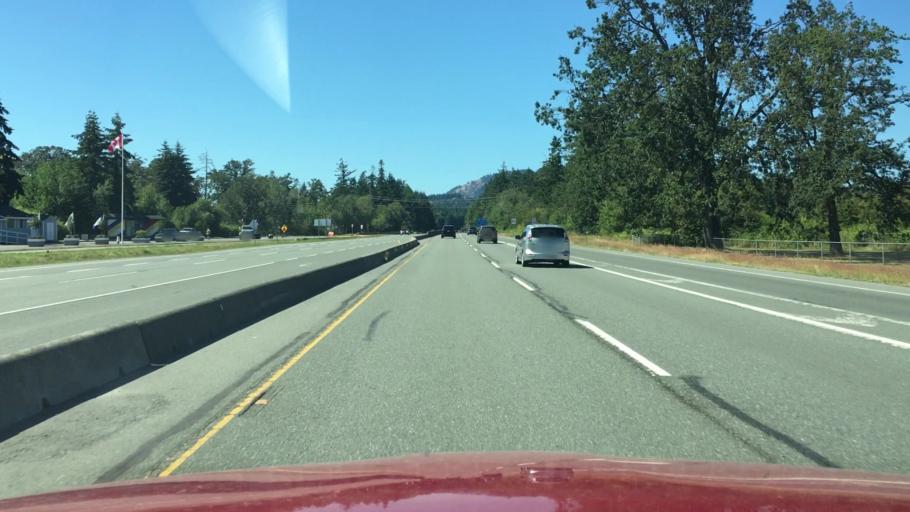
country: CA
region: British Columbia
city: North Saanich
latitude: 48.6641
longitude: -123.4186
